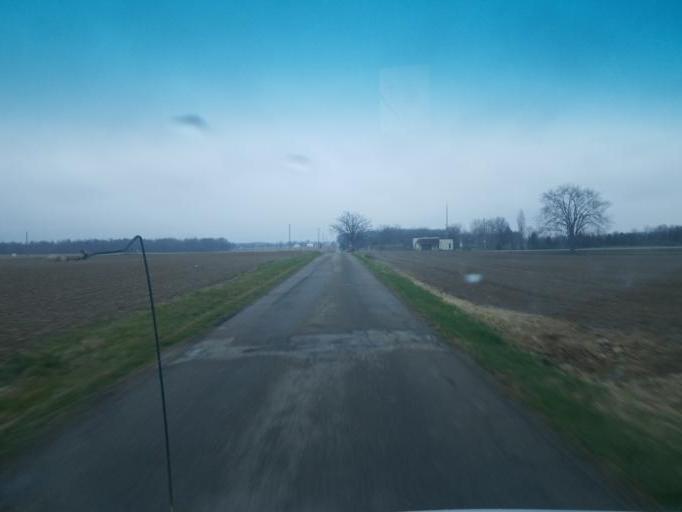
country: US
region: Ohio
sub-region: Defiance County
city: Hicksville
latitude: 41.3392
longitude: -84.7497
